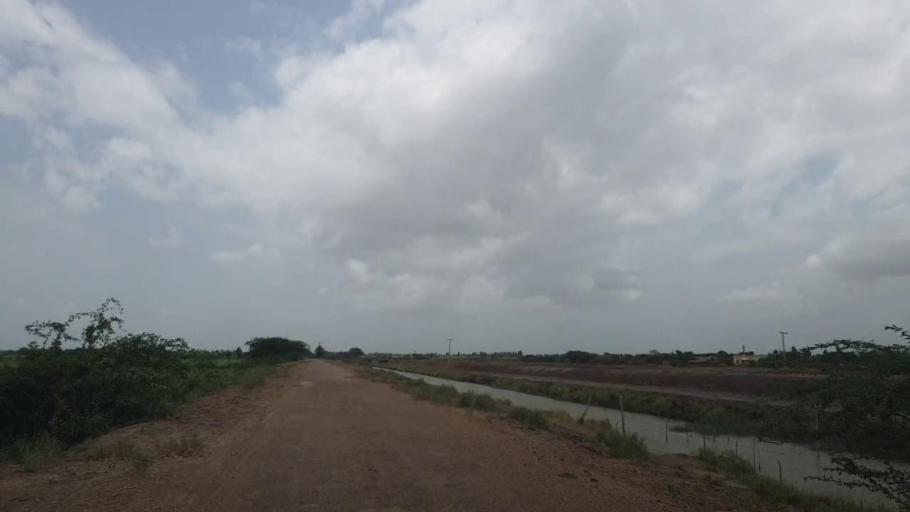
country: PK
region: Sindh
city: Badin
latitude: 24.6607
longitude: 68.8909
